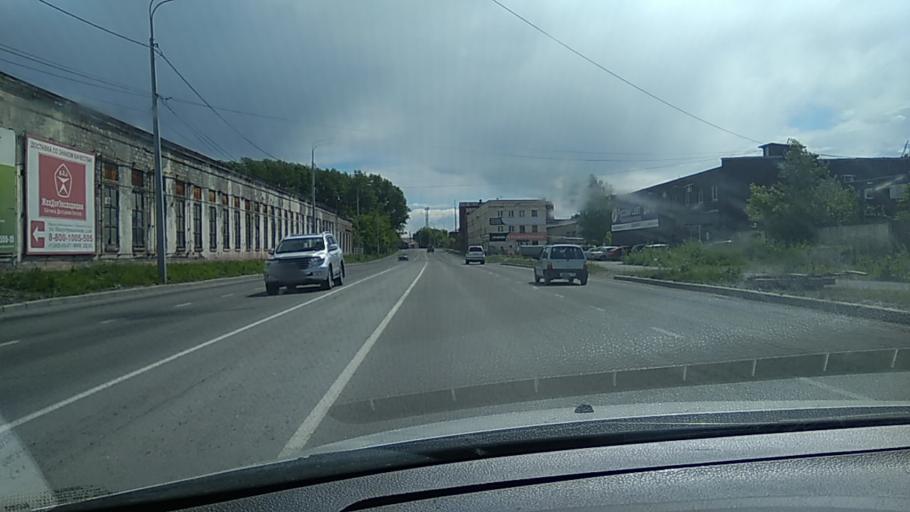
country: RU
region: Sverdlovsk
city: Nizhniy Tagil
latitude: 57.9167
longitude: 59.9899
